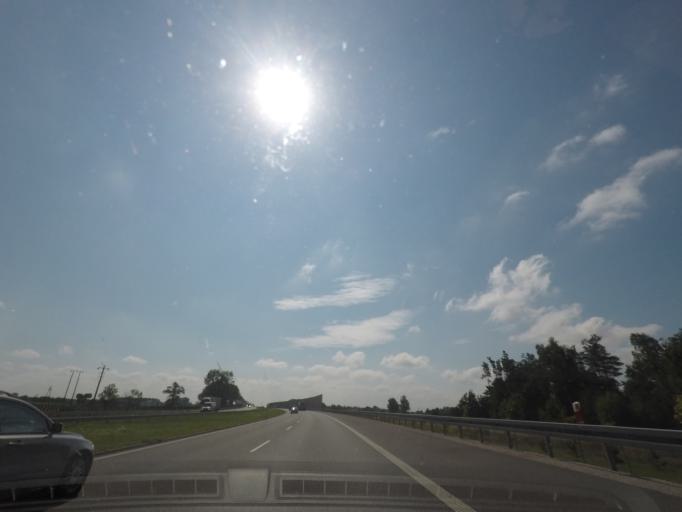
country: PL
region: Kujawsko-Pomorskie
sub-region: Powiat aleksandrowski
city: Raciazek
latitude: 52.8043
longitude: 18.8188
